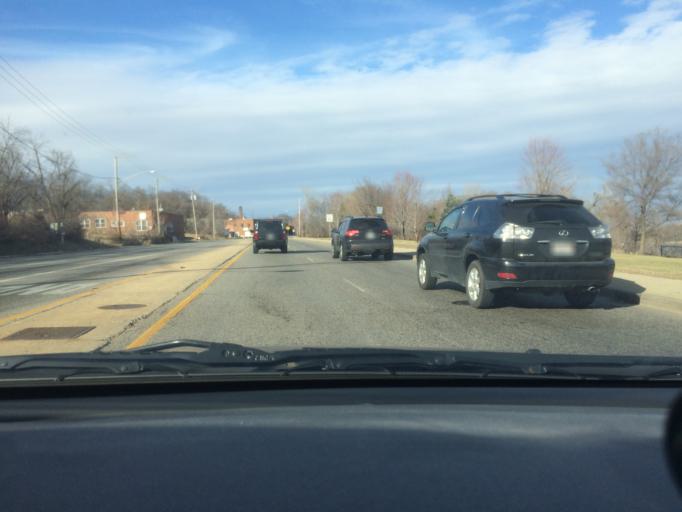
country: US
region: Illinois
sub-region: Kane County
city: Elgin
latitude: 42.0415
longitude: -88.2910
